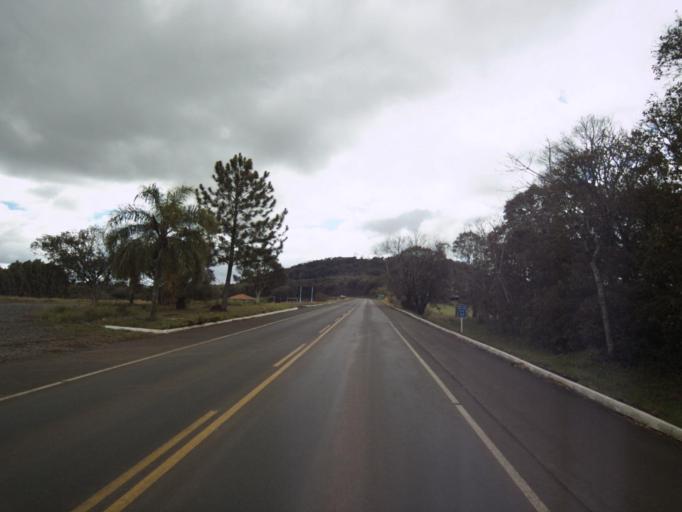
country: BR
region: Santa Catarina
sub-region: Concordia
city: Concordia
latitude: -27.3234
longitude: -51.9815
